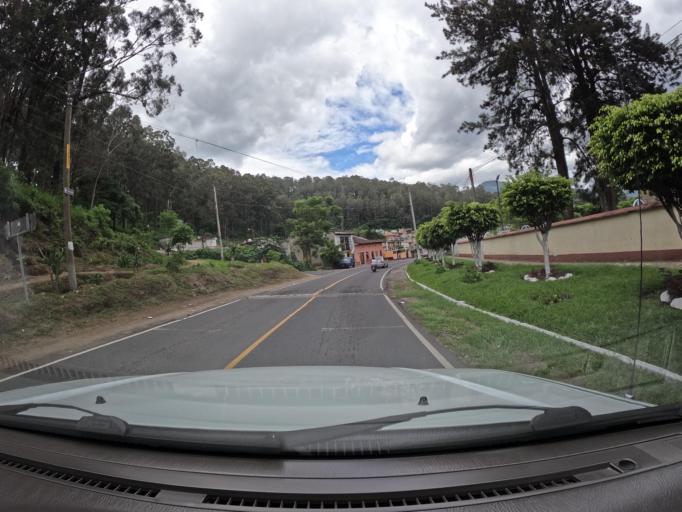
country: GT
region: Sacatepequez
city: Antigua Guatemala
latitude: 14.5663
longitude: -90.7362
